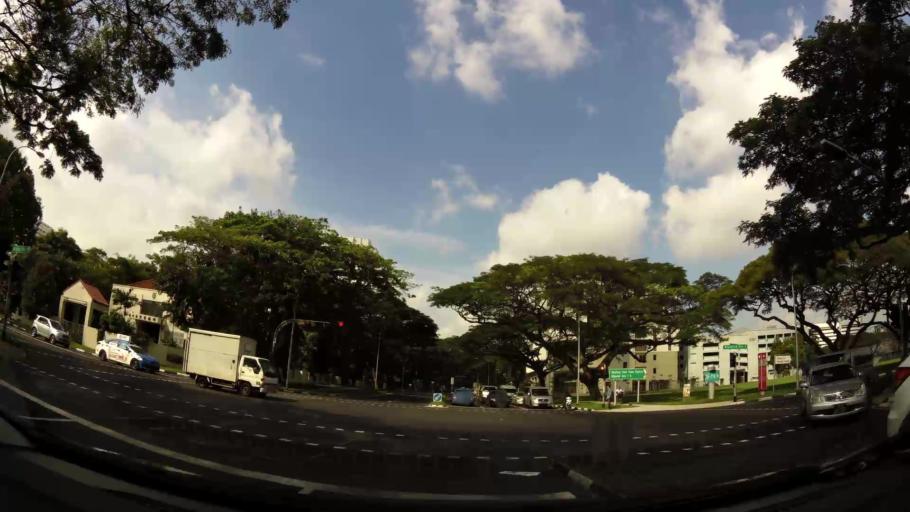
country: SG
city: Singapore
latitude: 1.3194
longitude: 103.8889
